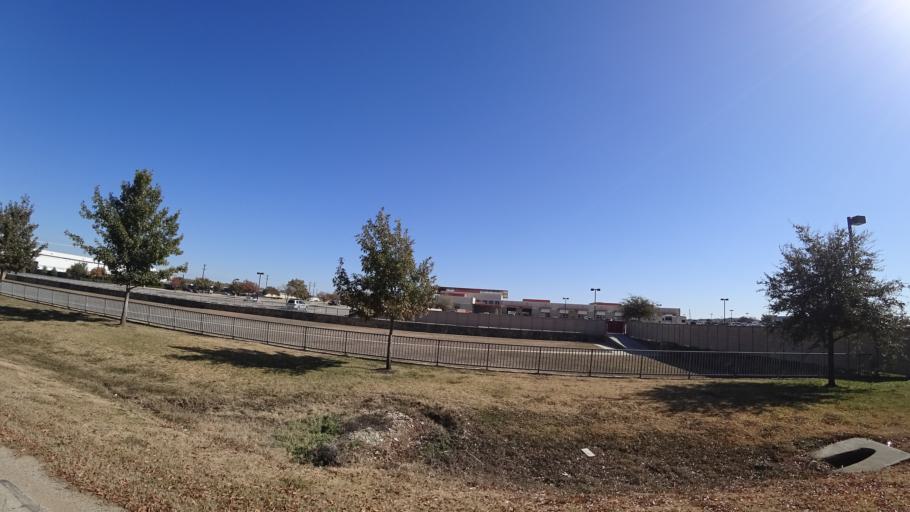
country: US
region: Texas
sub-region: Denton County
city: Lewisville
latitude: 33.0456
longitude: -96.9405
